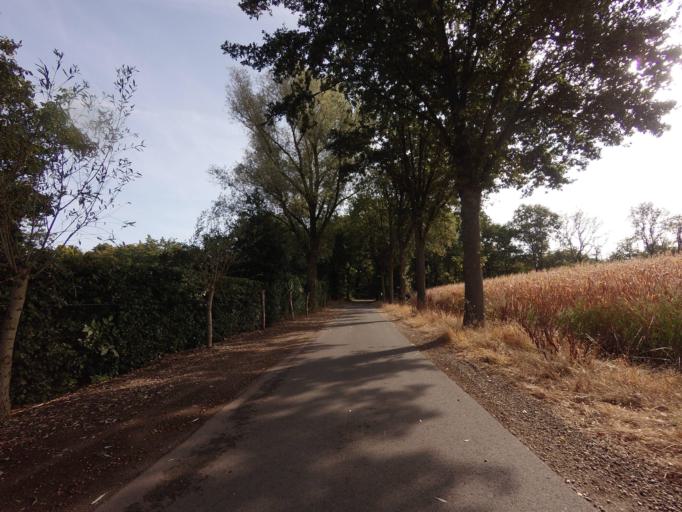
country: NL
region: North Brabant
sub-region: Gemeente Mill en Sint Hubert
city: Wilbertoord
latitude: 51.6658
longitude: 5.7710
